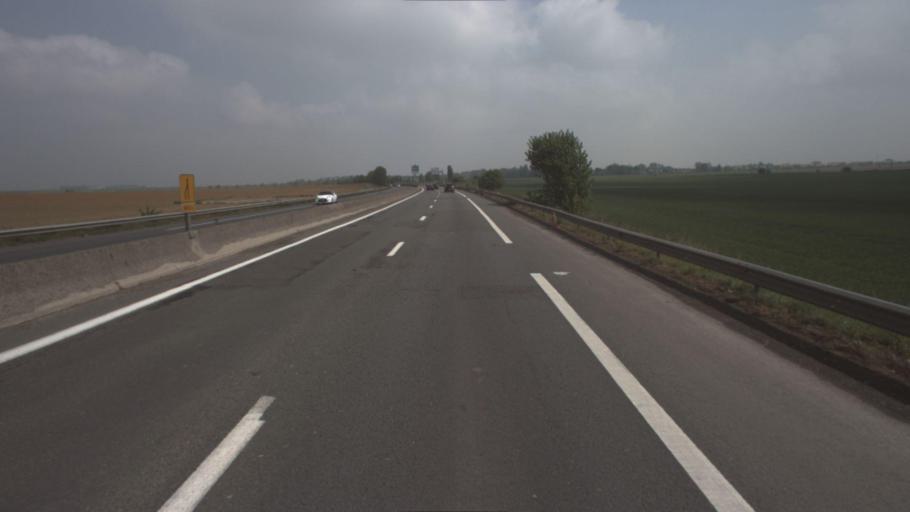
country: FR
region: Picardie
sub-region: Departement de l'Oise
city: Lagny-le-Sec
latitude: 49.0789
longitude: 2.7265
